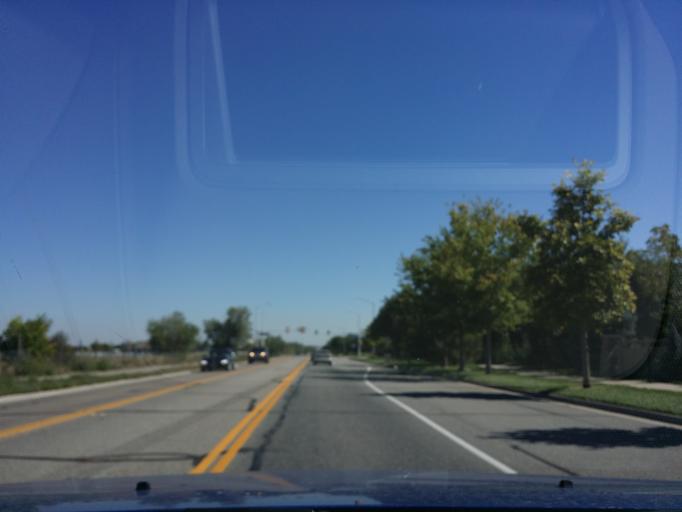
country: US
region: Colorado
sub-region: Broomfield County
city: Broomfield
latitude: 39.9577
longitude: -105.0246
